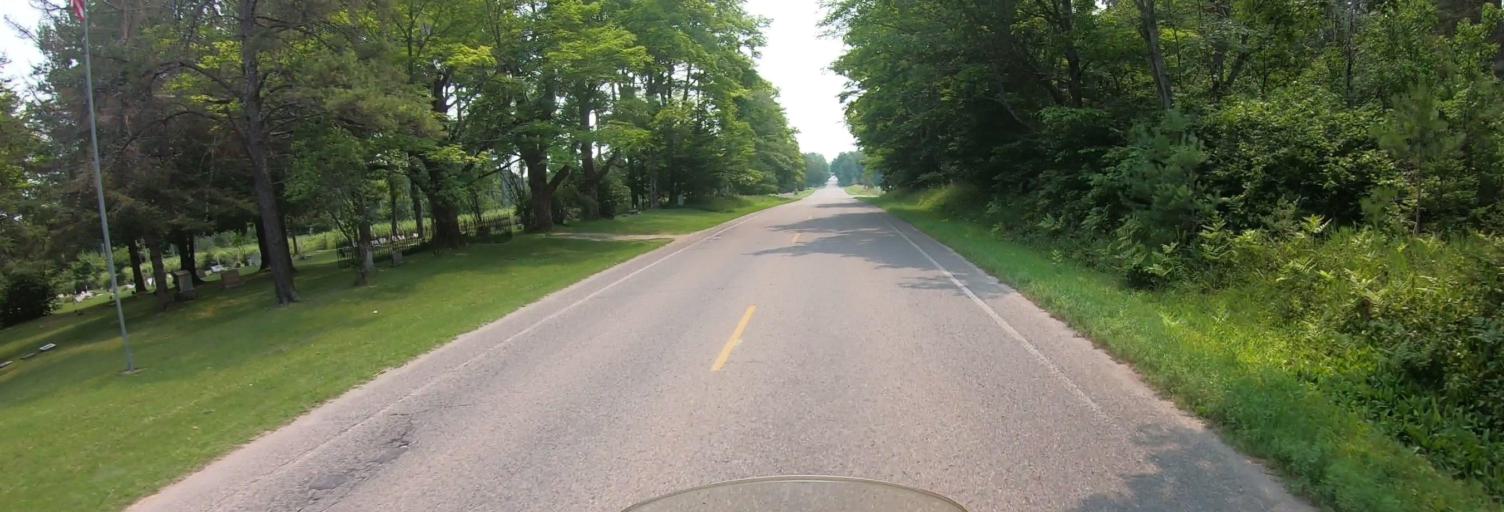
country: CA
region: Ontario
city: Thessalon
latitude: 46.0072
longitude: -83.7385
